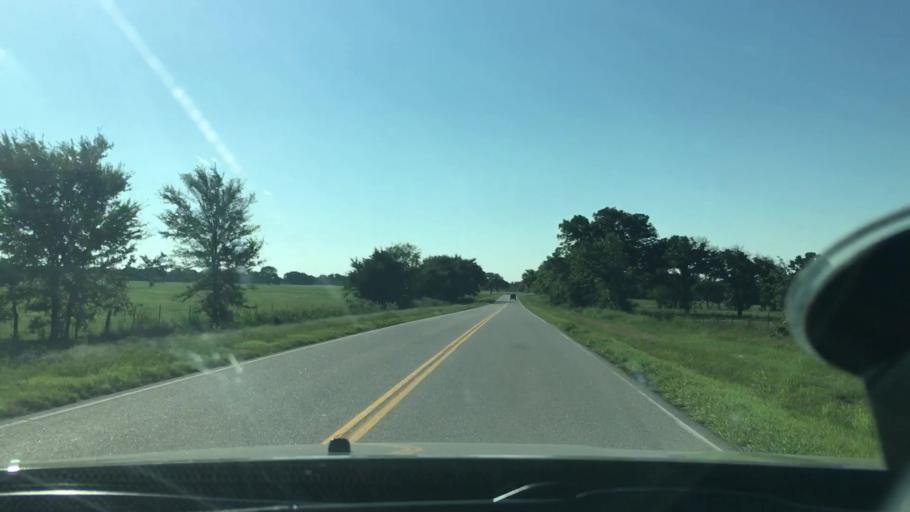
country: US
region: Oklahoma
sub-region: Johnston County
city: Tishomingo
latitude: 34.1838
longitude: -96.7203
